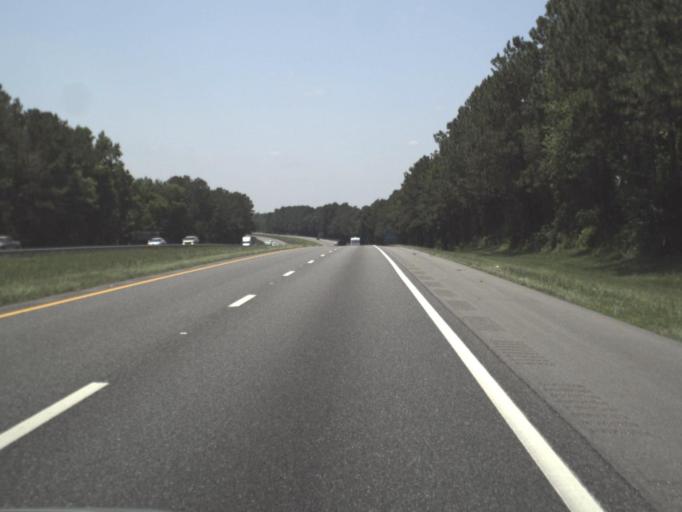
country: US
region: Florida
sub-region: Suwannee County
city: Wellborn
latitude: 30.2612
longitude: -82.7324
